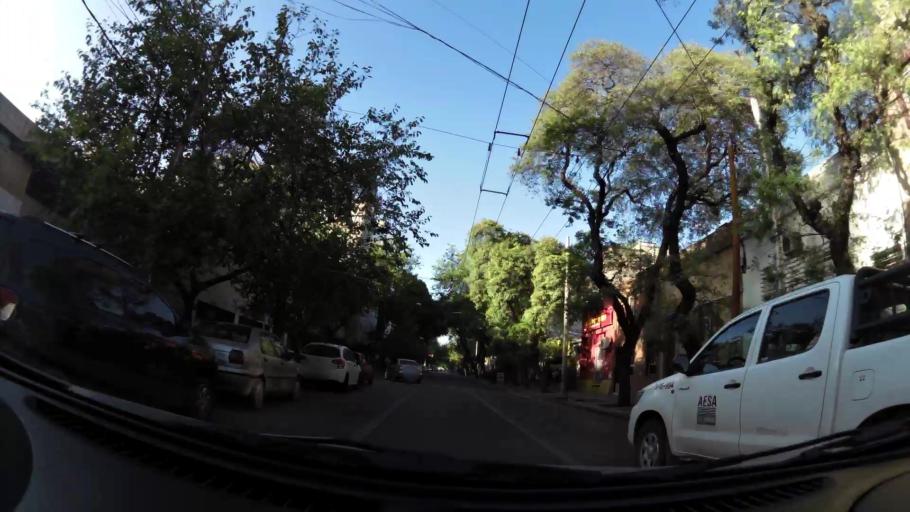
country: AR
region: Mendoza
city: Mendoza
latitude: -32.8952
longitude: -68.8421
